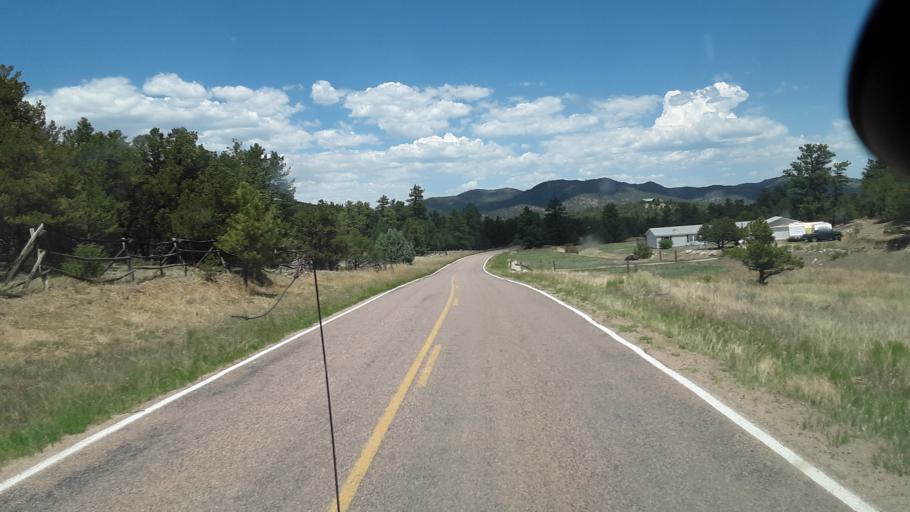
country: US
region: Colorado
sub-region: Custer County
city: Westcliffe
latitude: 38.3392
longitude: -105.4850
